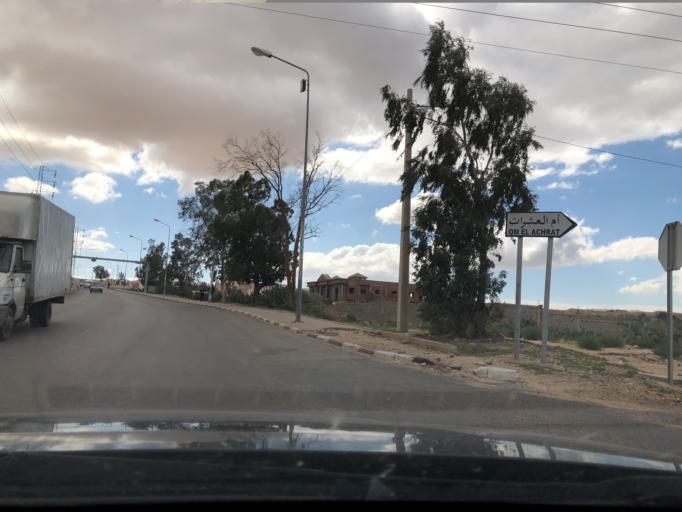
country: TN
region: Al Qasrayn
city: Kasserine
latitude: 35.1735
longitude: 8.7937
